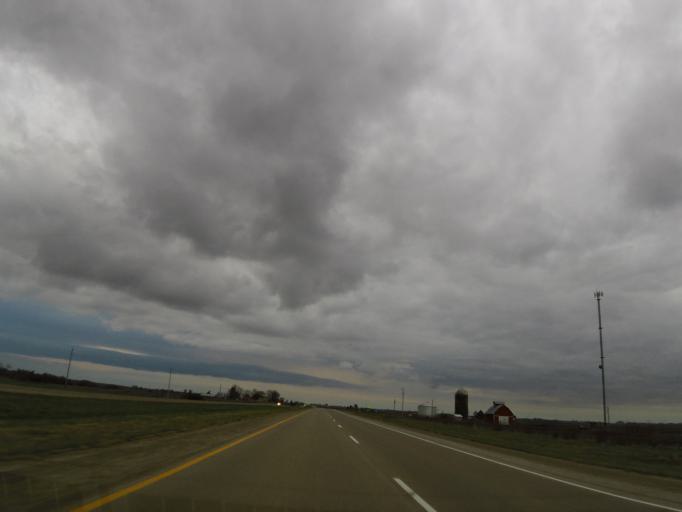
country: US
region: Iowa
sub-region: Henry County
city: Mount Pleasant
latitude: 40.8157
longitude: -91.5648
